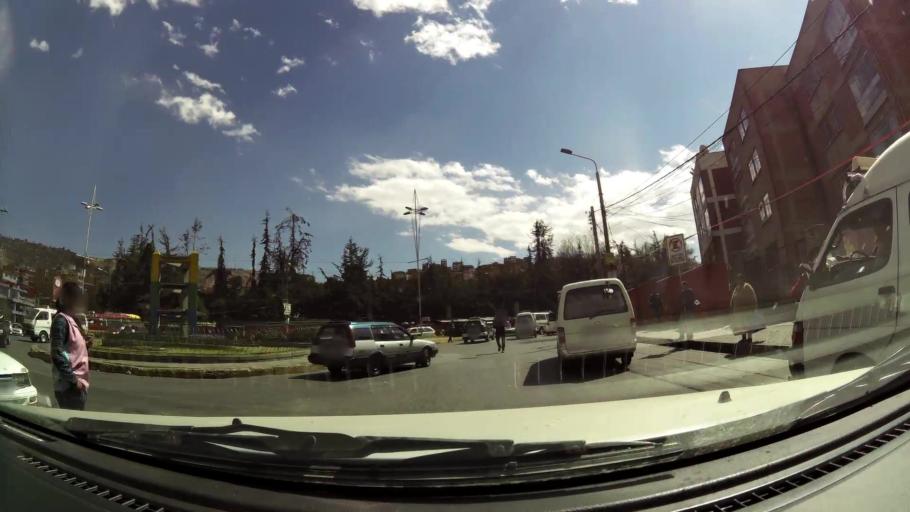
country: BO
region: La Paz
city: La Paz
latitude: -16.4925
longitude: -68.1434
